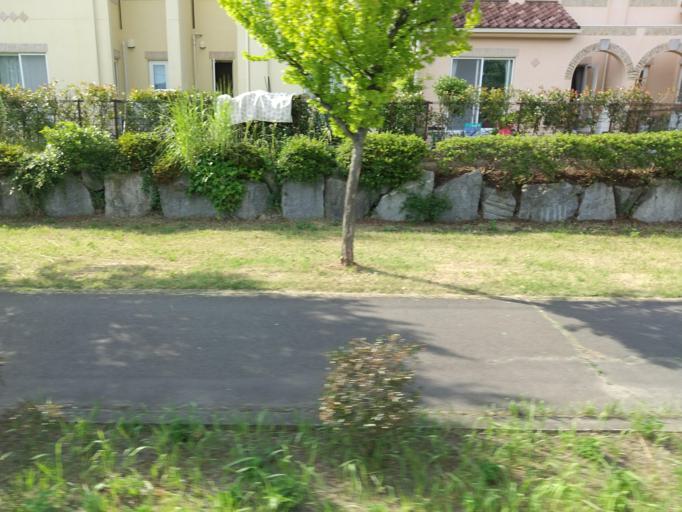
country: JP
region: Miyagi
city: Sendai
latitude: 38.2579
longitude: 140.7594
